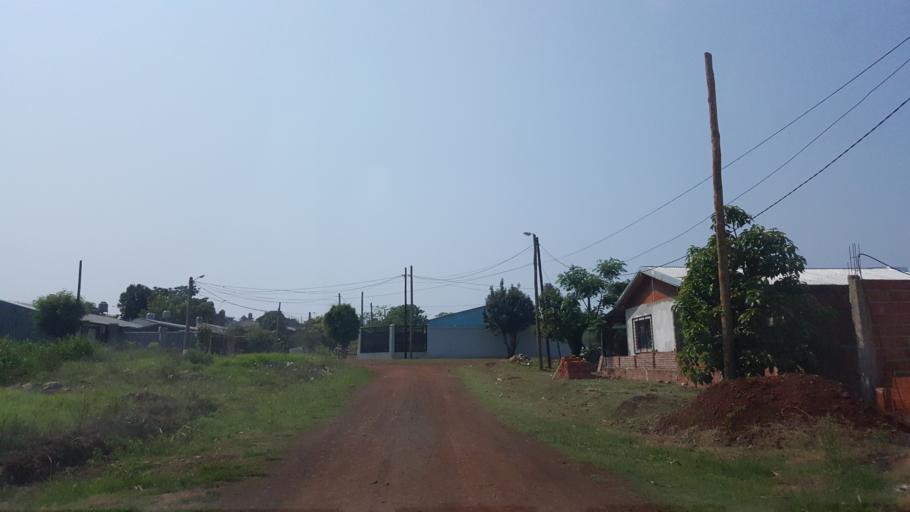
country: AR
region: Misiones
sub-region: Departamento de Capital
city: Posadas
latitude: -27.4187
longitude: -55.9563
